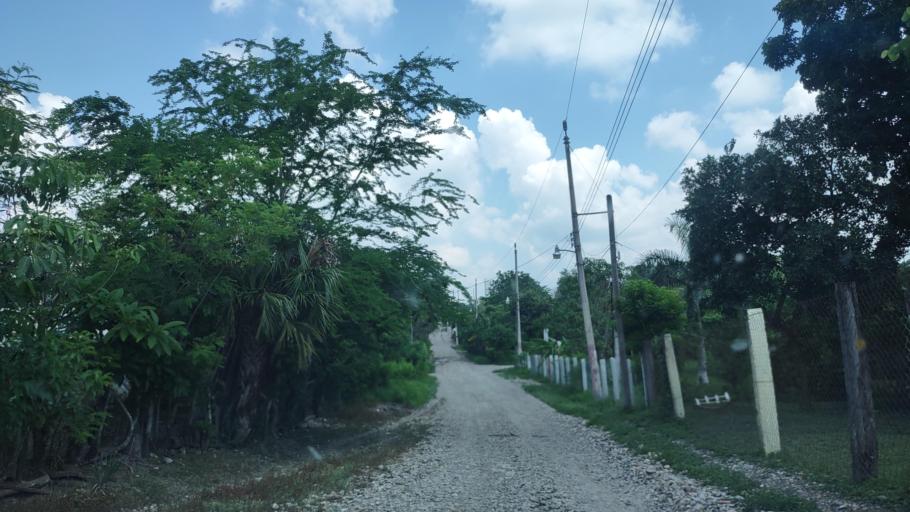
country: MX
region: Veracruz
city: Tempoal de Sanchez
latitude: 21.5460
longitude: -98.2763
